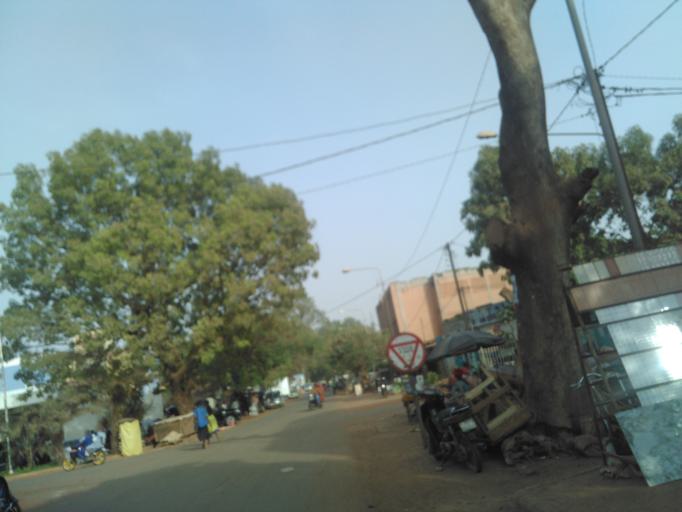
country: BF
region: High-Basins
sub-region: Province du Houet
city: Bobo-Dioulasso
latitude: 11.1735
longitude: -4.3033
